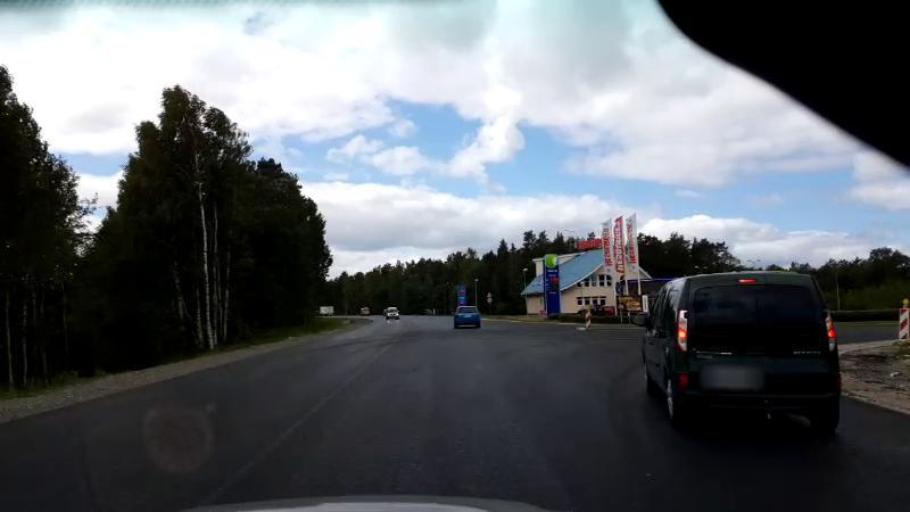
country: LV
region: Salacgrivas
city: Ainazi
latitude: 57.8473
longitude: 24.3519
